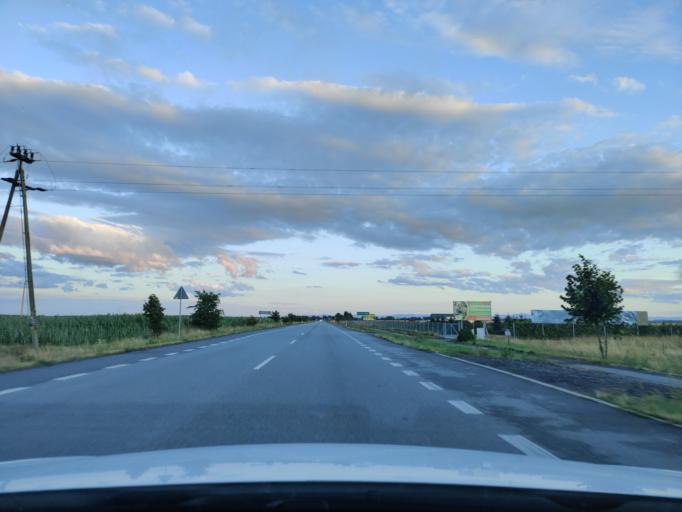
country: PL
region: Opole Voivodeship
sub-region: Powiat brzeski
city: Grodkow
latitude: 50.6726
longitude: 17.3880
